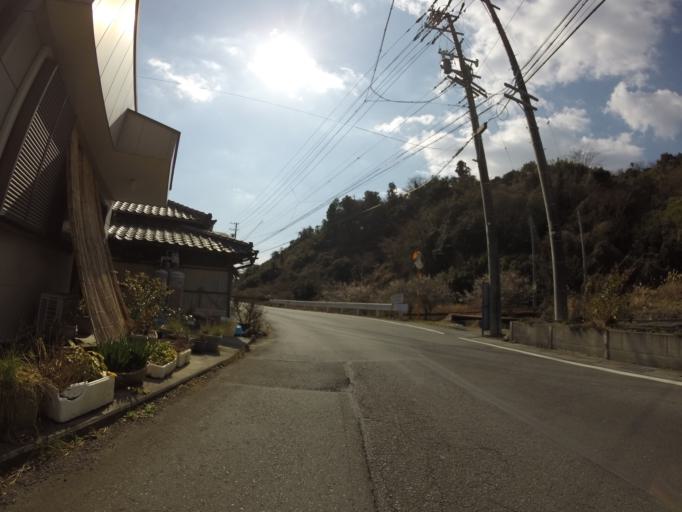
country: JP
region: Shizuoka
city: Shizuoka-shi
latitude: 35.0608
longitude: 138.4833
